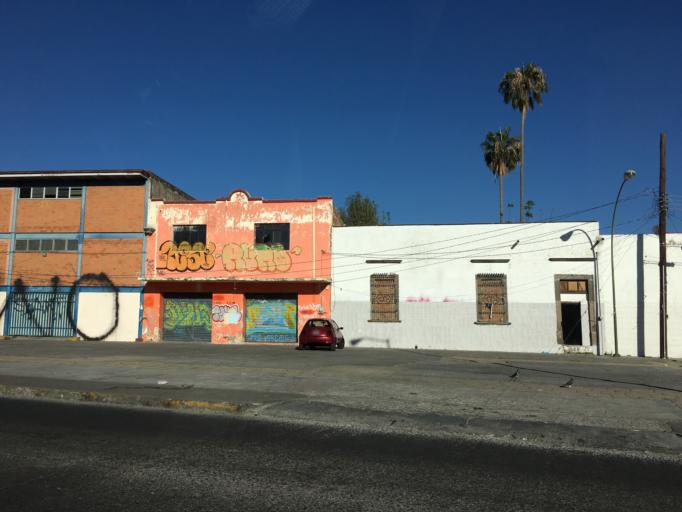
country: MX
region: Jalisco
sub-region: Zapopan
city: Zapopan
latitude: 20.6914
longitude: -103.3538
